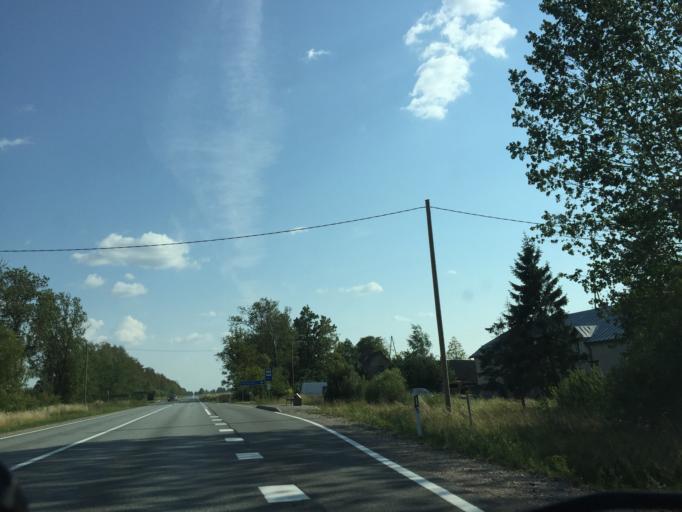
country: LV
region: Jelgava
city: Jelgava
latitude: 56.4514
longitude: 23.6904
